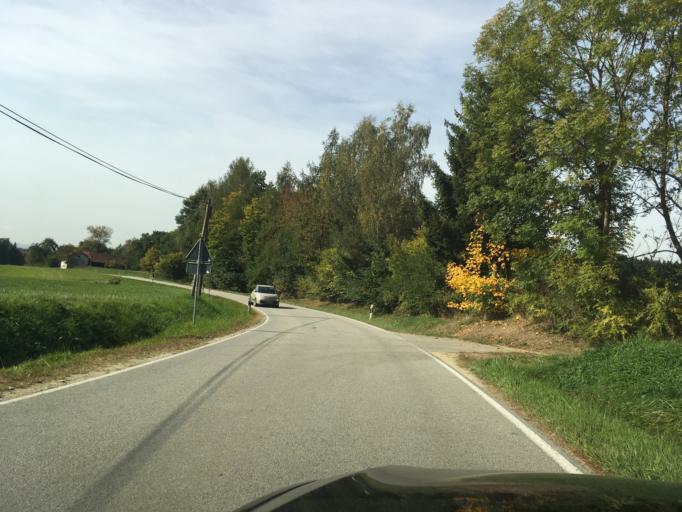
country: DE
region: Bavaria
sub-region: Lower Bavaria
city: Hofkirchen
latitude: 48.6985
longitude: 13.1284
